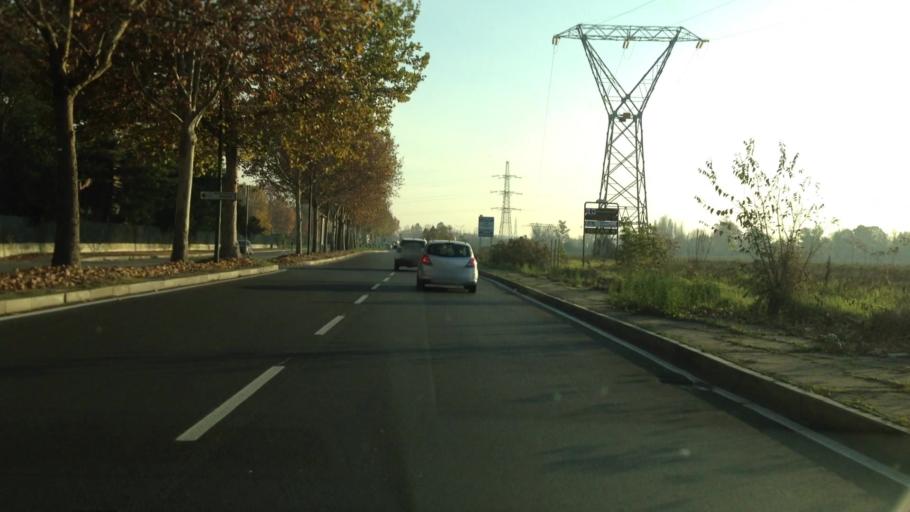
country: IT
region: Piedmont
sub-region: Provincia di Torino
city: Savonera
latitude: 45.1027
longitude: 7.6248
